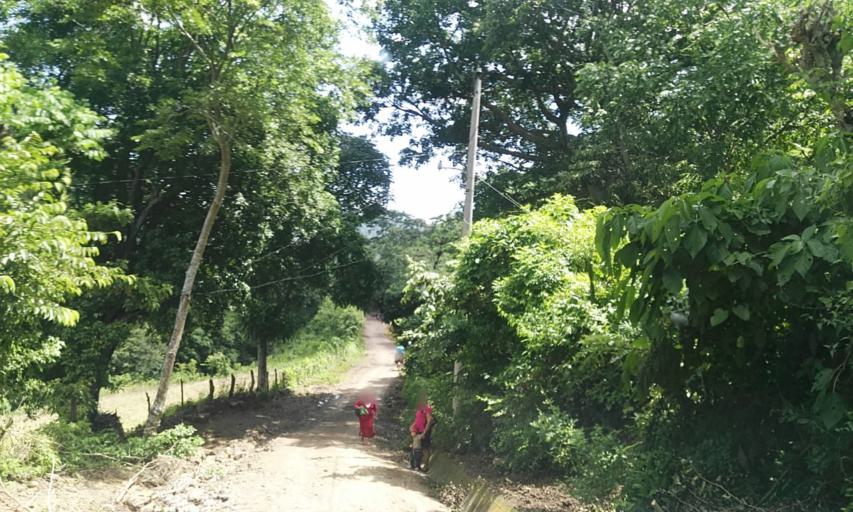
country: NI
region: Matagalpa
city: Terrabona
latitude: 12.7416
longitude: -85.9229
